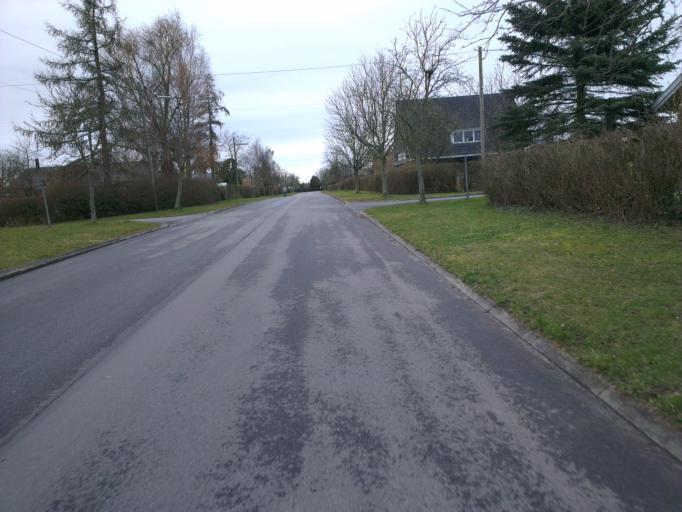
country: DK
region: Capital Region
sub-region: Frederikssund Kommune
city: Frederikssund
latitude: 55.8212
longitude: 12.0839
